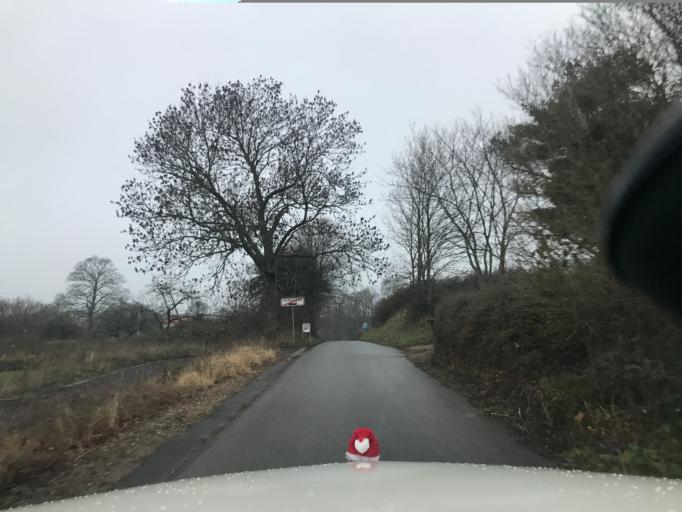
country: DK
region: South Denmark
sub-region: Sonderborg Kommune
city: Grasten
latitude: 54.8820
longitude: 9.5674
